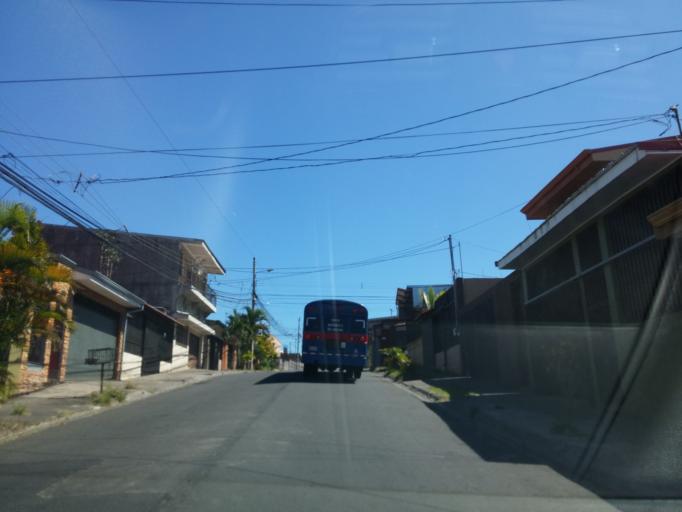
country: CR
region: Alajuela
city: Alajuela
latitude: 10.0127
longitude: -84.1982
